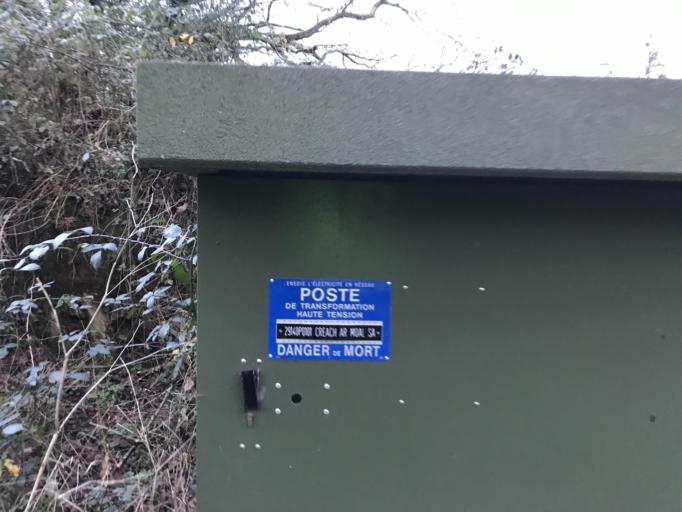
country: FR
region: Brittany
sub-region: Departement du Finistere
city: Loperhet
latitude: 48.3670
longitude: -4.3162
